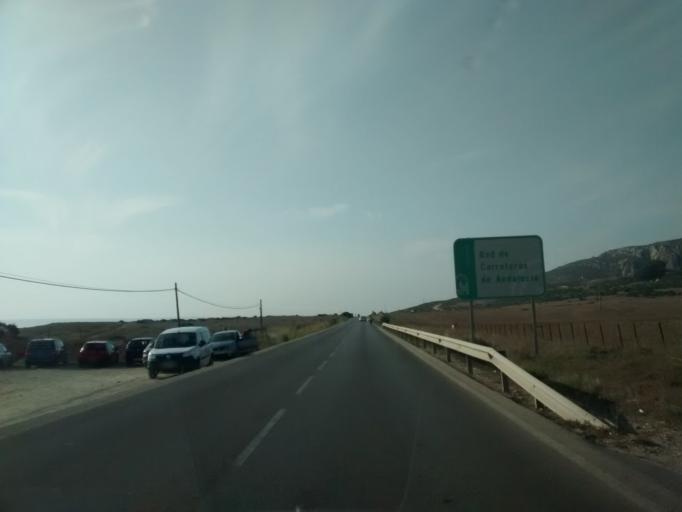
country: ES
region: Andalusia
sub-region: Provincia de Cadiz
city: Zahara de los Atunes
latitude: 36.1409
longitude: -5.8525
